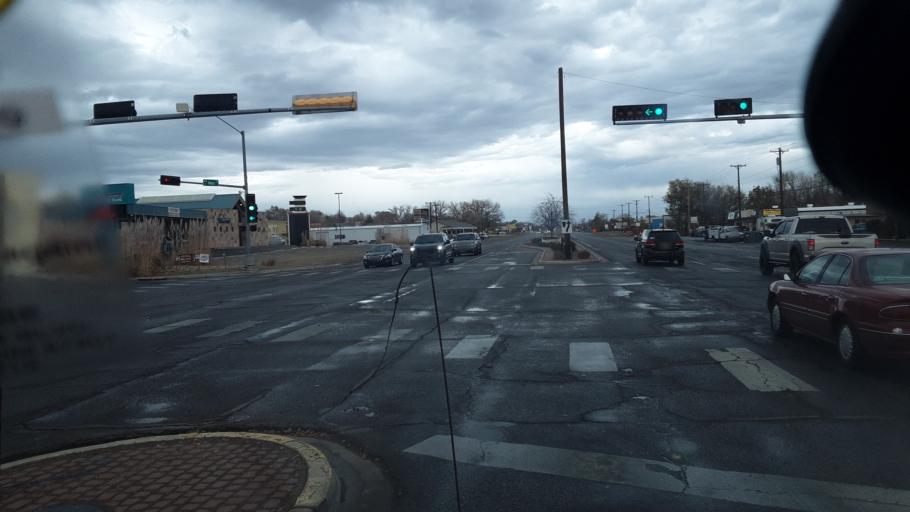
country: US
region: New Mexico
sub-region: San Juan County
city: Flora Vista
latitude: 36.7735
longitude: -108.1349
